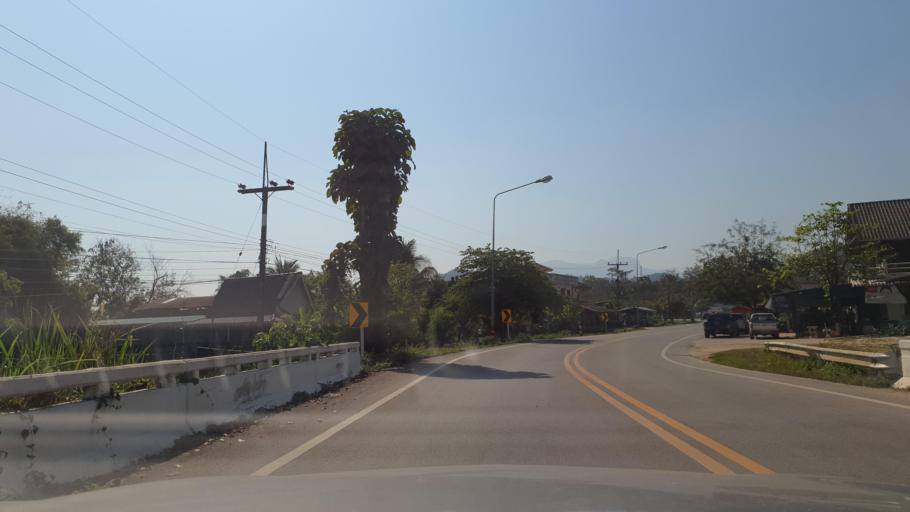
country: TH
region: Chiang Rai
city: Mae Lao
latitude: 19.8347
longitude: 99.6972
